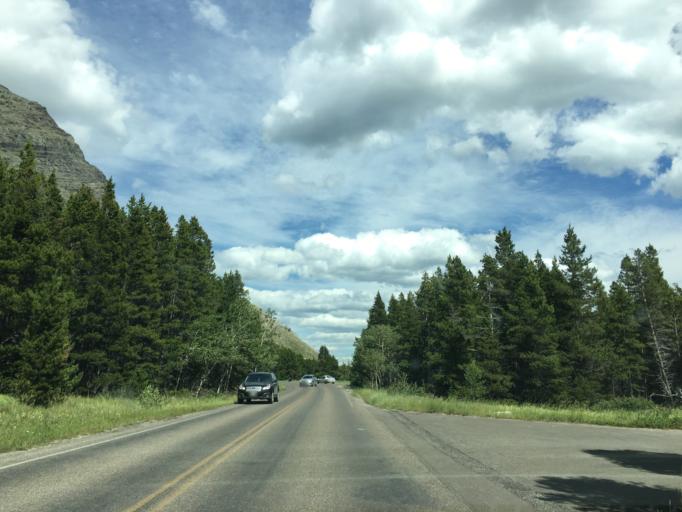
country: CA
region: Alberta
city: Cardston
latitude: 48.7992
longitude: -113.6658
